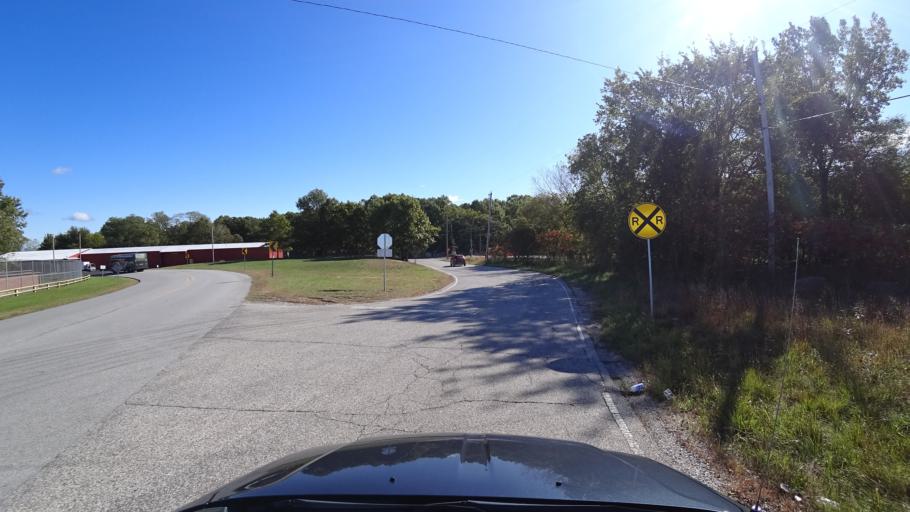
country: US
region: Indiana
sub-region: LaPorte County
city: Michigan City
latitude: 41.7008
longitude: -86.9152
